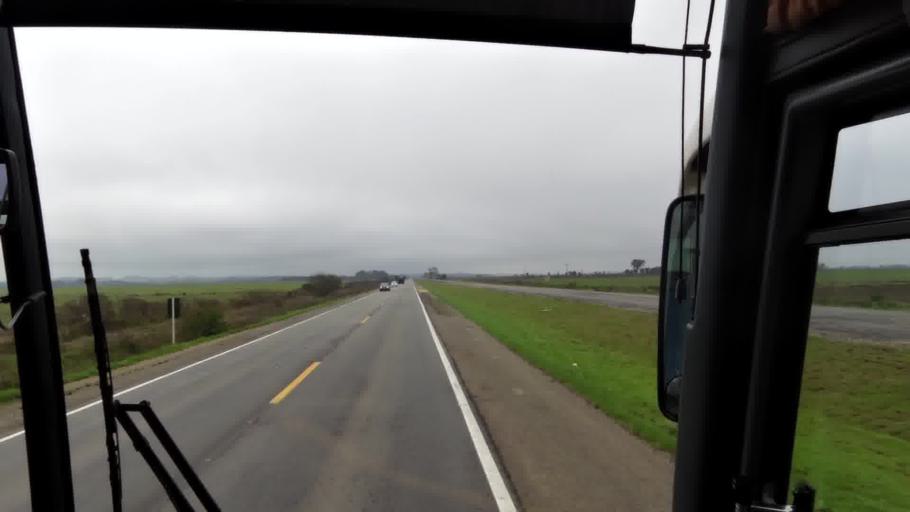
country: BR
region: Rio Grande do Sul
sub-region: Pelotas
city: Pelotas
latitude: -31.5962
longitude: -52.2878
